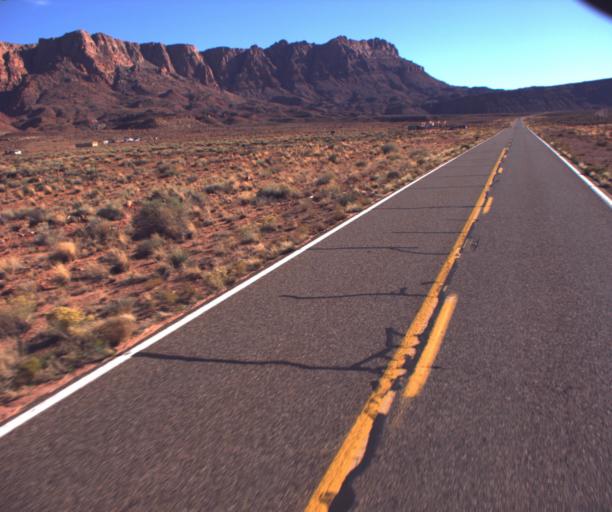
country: US
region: Arizona
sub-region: Coconino County
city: LeChee
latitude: 36.7418
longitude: -111.6378
